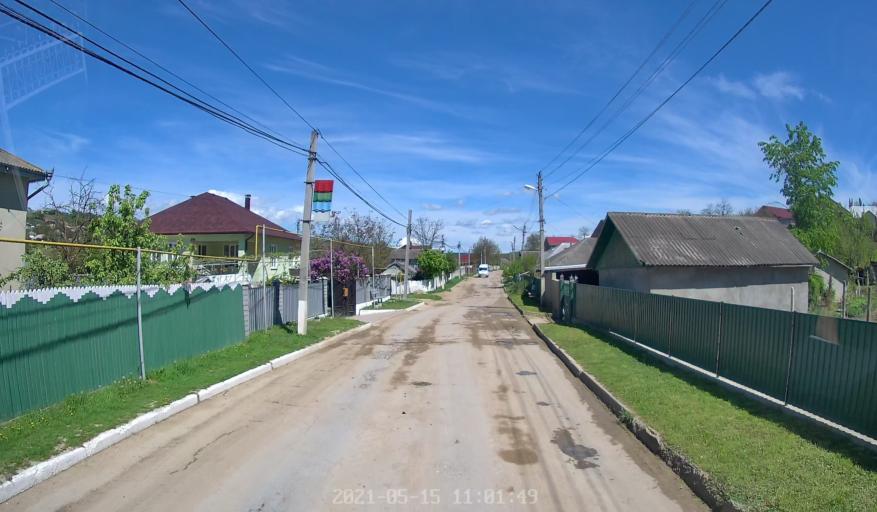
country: MD
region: Hincesti
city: Hincesti
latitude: 46.8278
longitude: 28.6767
